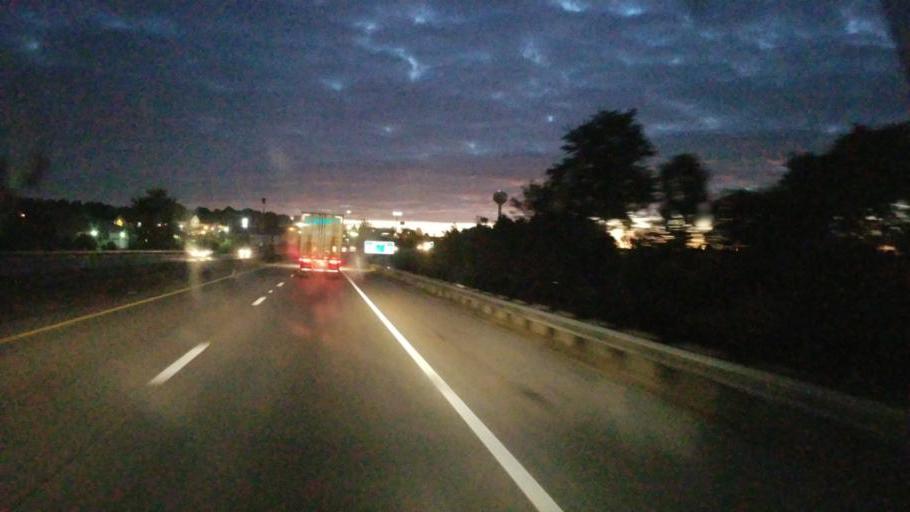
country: US
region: Ohio
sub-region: Medina County
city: Seville
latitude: 41.0325
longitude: -81.8750
